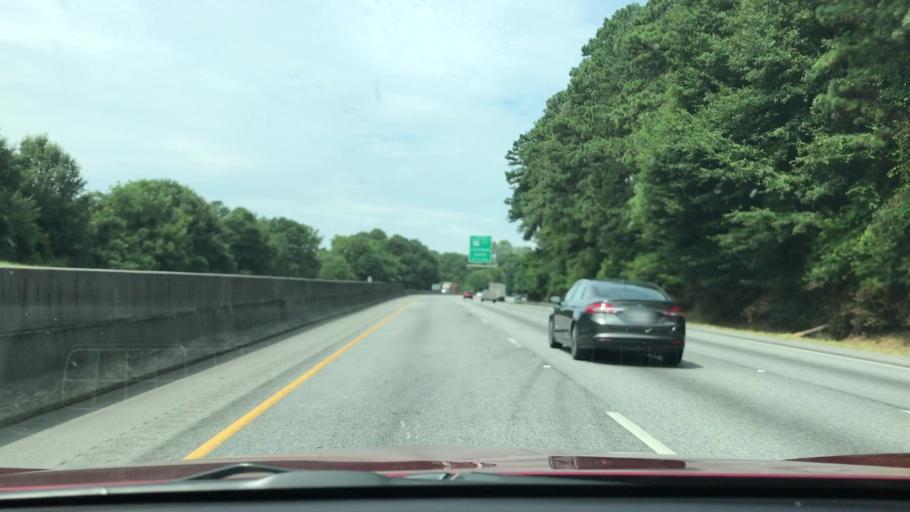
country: US
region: Georgia
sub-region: Newton County
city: Oxford
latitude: 33.6096
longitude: -83.8682
